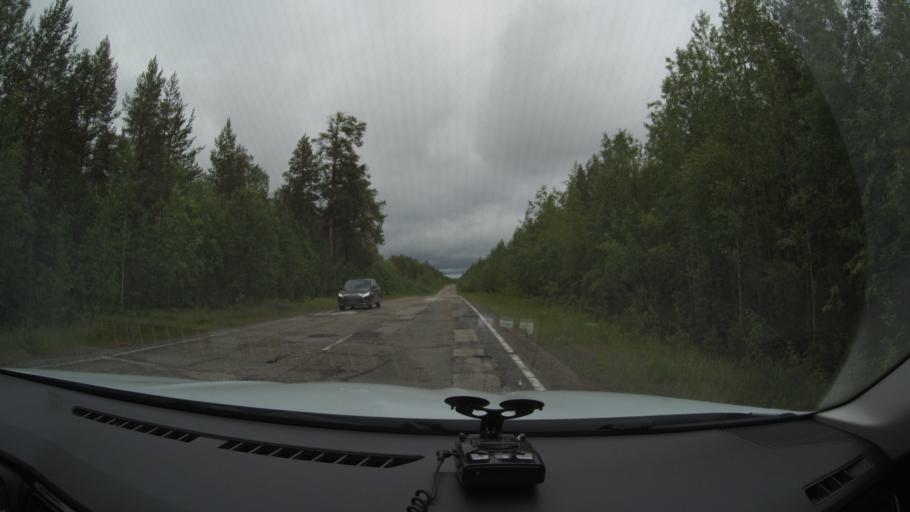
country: RU
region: Komi Republic
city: Nizhniy Odes
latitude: 63.6601
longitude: 54.6789
